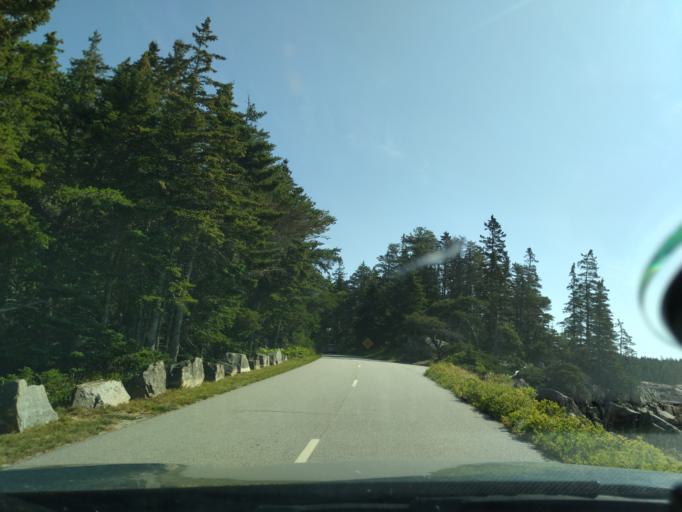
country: US
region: Maine
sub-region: Hancock County
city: Gouldsboro
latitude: 44.3626
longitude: -68.0397
